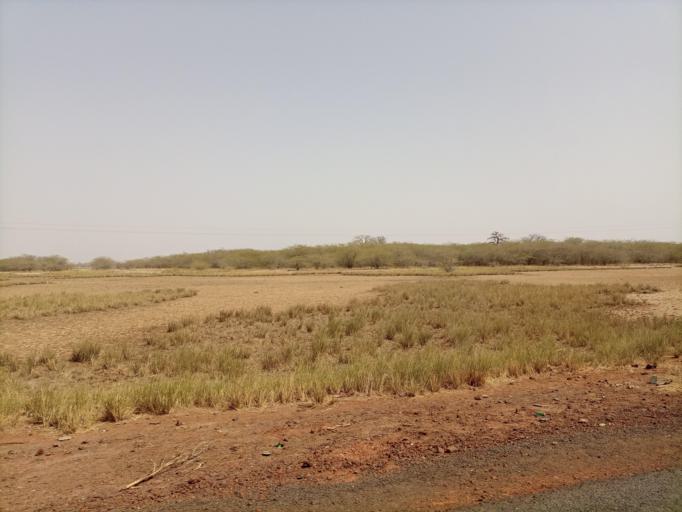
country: SN
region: Fatick
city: Foundiougne
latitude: 14.1821
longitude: -16.4565
